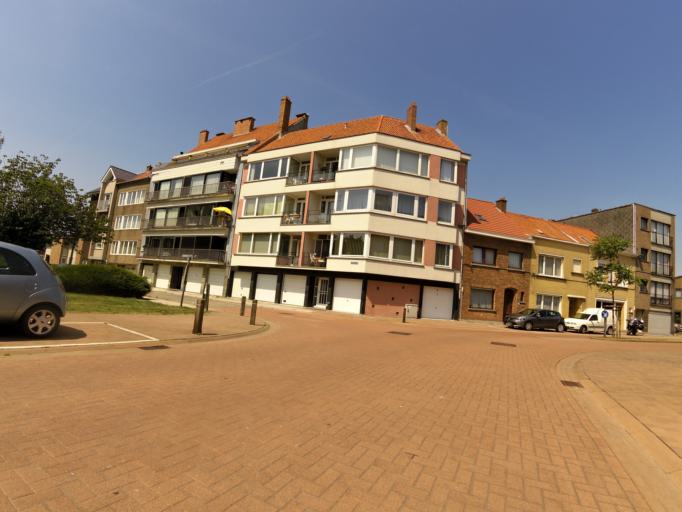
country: BE
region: Flanders
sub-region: Provincie West-Vlaanderen
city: Ostend
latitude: 51.2146
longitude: 2.8997
